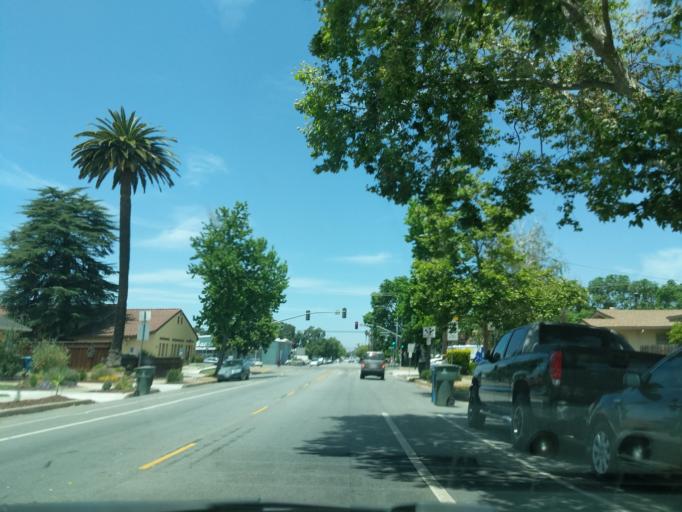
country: US
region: California
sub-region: Santa Clara County
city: Gilroy
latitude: 37.0132
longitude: -121.5743
